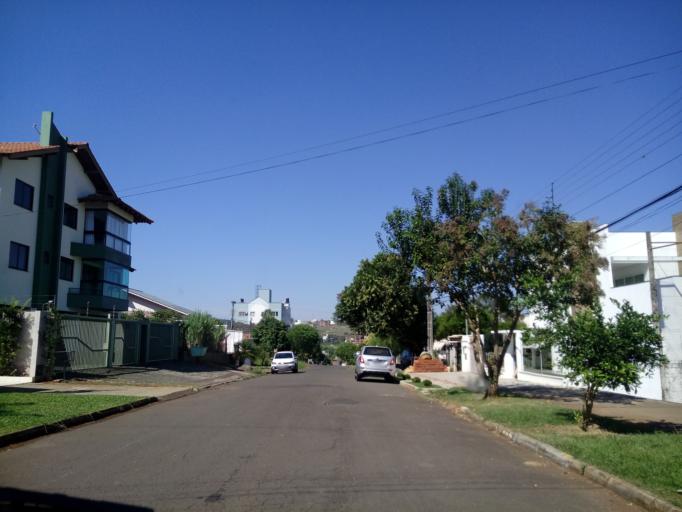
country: BR
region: Santa Catarina
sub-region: Chapeco
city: Chapeco
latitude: -27.0921
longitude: -52.6004
